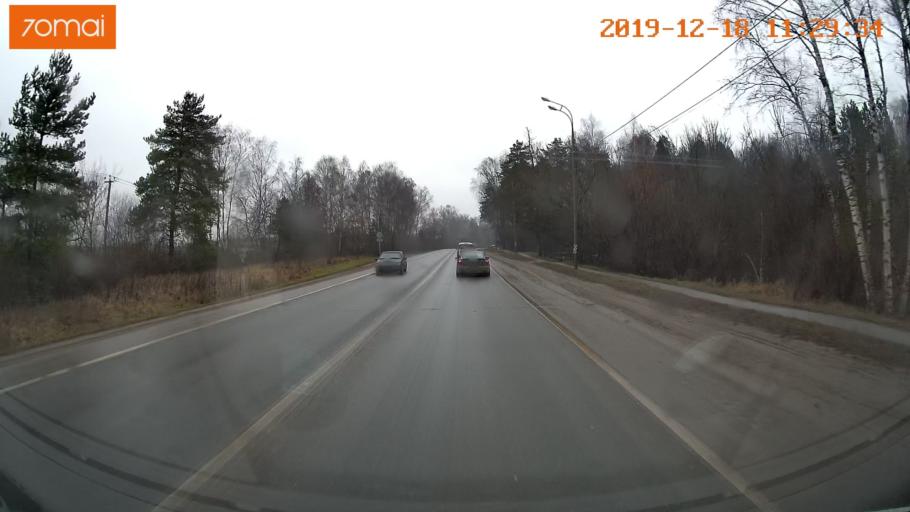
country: RU
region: Moskovskaya
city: Bol'shiye Vyazemy
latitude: 55.6505
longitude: 36.9715
